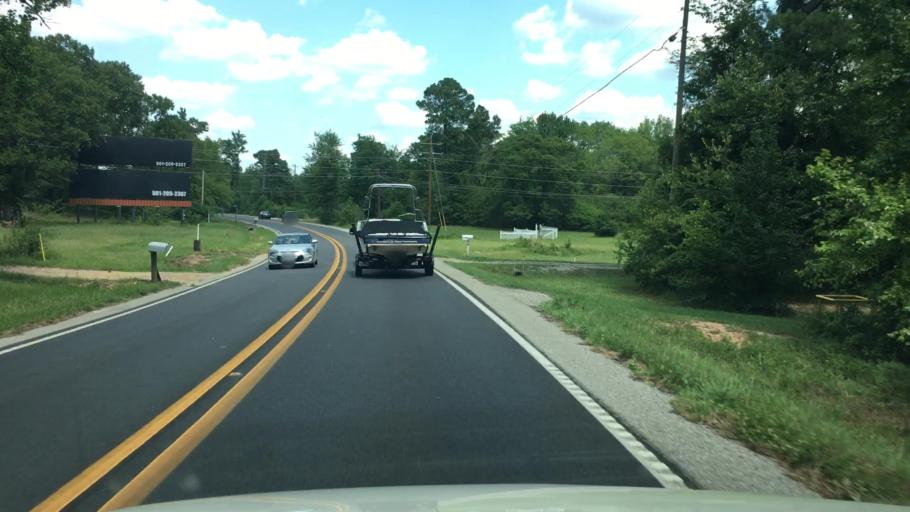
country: US
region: Arkansas
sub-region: Garland County
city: Lake Hamilton
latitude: 34.3956
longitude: -93.1072
